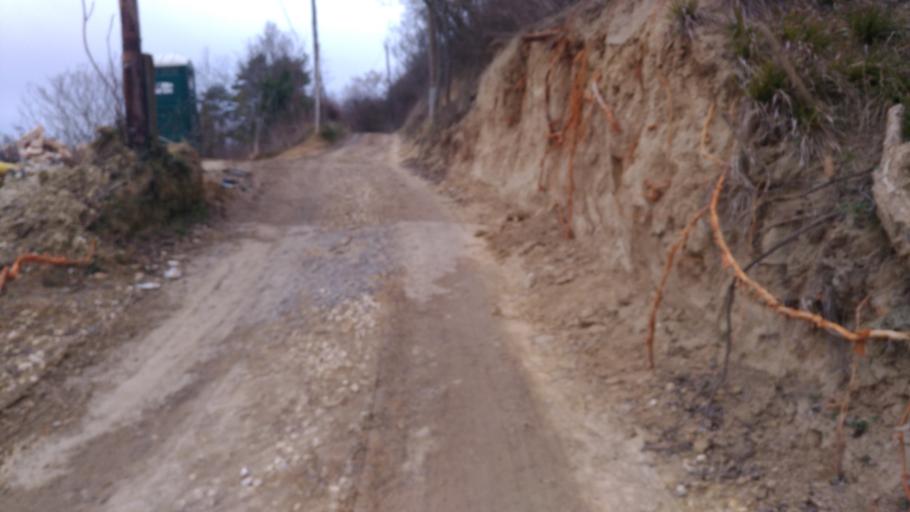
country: HU
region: Pest
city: Urom
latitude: 47.5848
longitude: 19.0271
